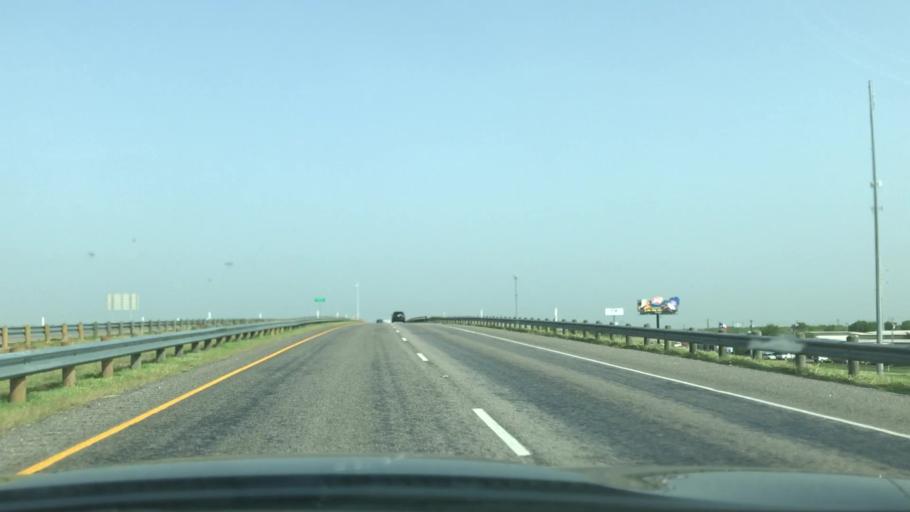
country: US
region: Texas
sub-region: Kaufman County
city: Talty
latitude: 32.7376
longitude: -96.3543
